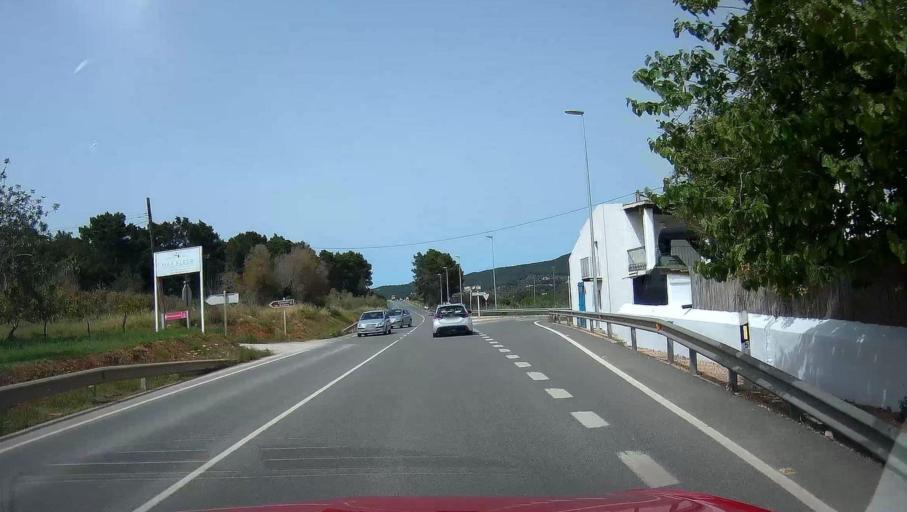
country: ES
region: Balearic Islands
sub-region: Illes Balears
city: Sant Joan de Labritja
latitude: 39.0332
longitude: 1.4903
